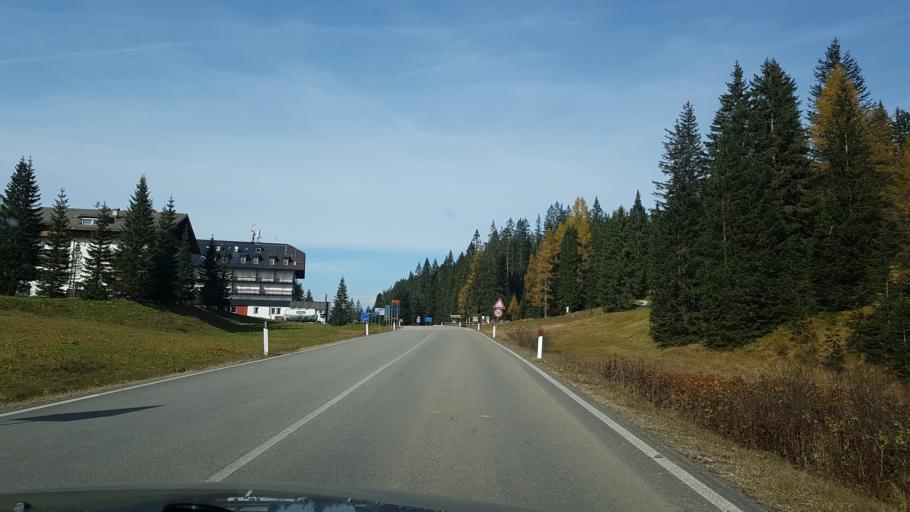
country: IT
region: Trentino-Alto Adige
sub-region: Bolzano
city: Sesto
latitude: 46.6547
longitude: 12.4218
